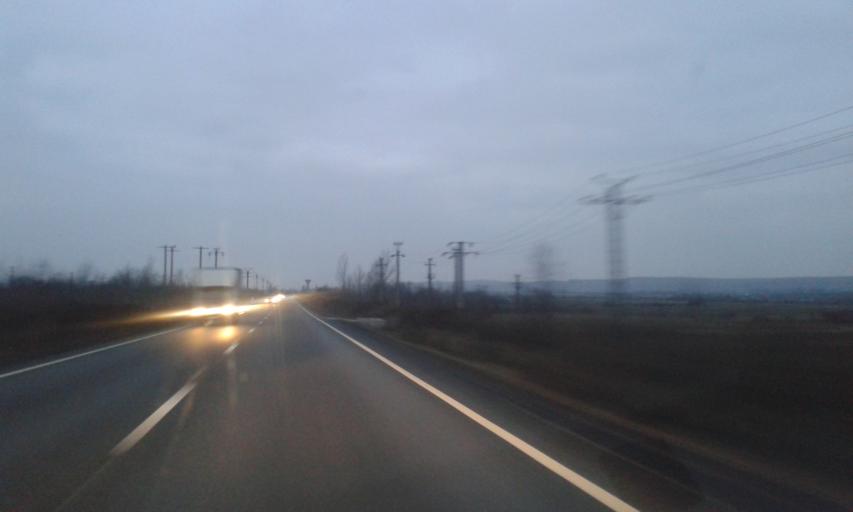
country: RO
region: Gorj
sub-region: Comuna Turcinesti
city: Turcinesti
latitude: 45.1224
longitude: 23.3542
